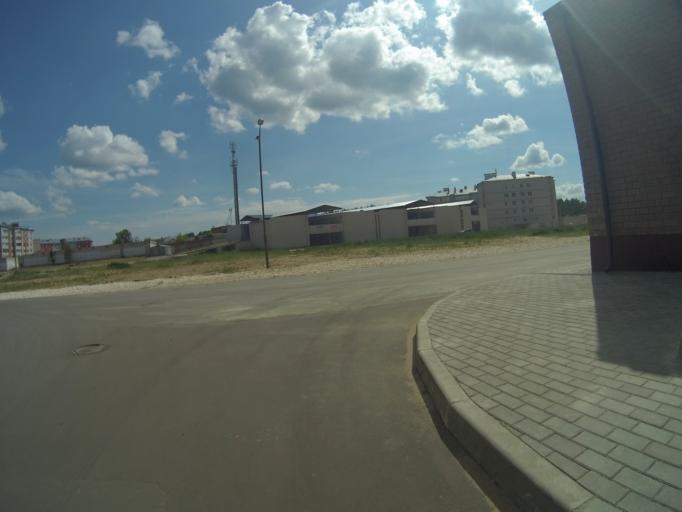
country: RU
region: Vladimir
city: Kommunar
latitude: 56.1089
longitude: 40.4379
